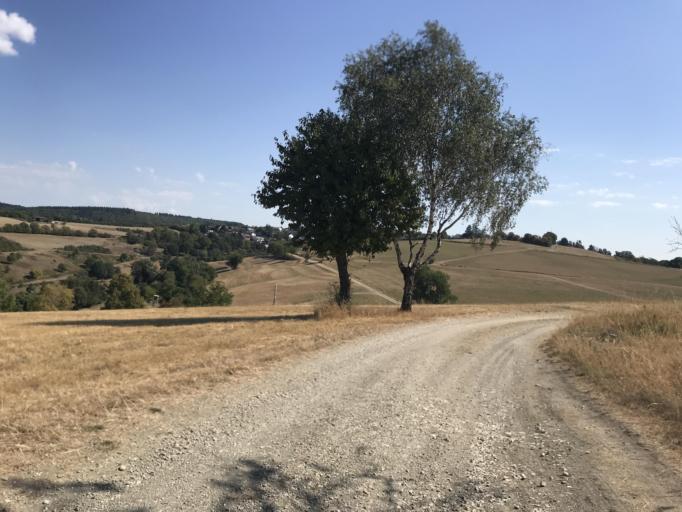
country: DE
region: Rheinland-Pfalz
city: Trechtingshausen
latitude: 50.0497
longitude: 7.8769
